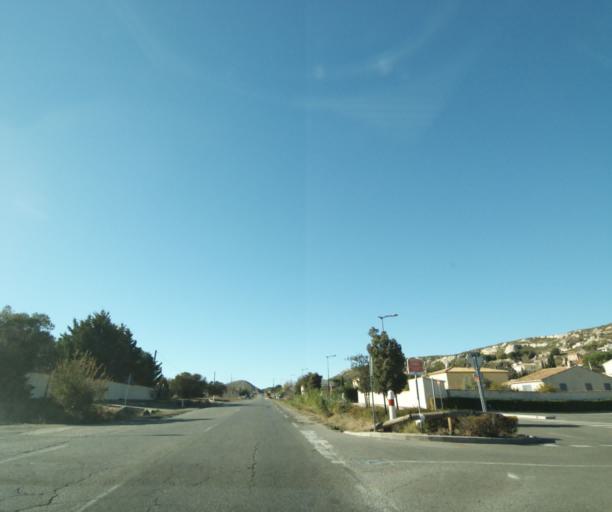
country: FR
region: Provence-Alpes-Cote d'Azur
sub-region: Departement des Bouches-du-Rhone
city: Le Rove
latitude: 43.3688
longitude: 5.2545
